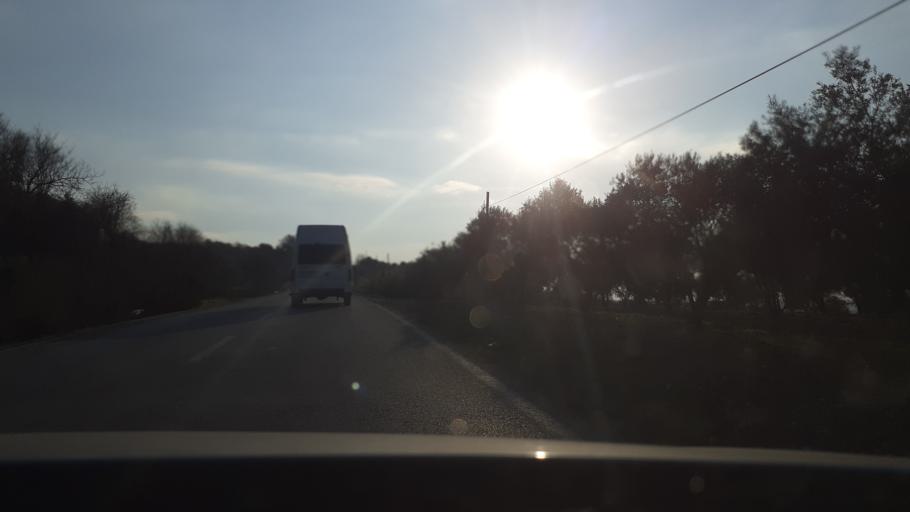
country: TR
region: Hatay
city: Oymakli
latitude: 36.1232
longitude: 36.3077
